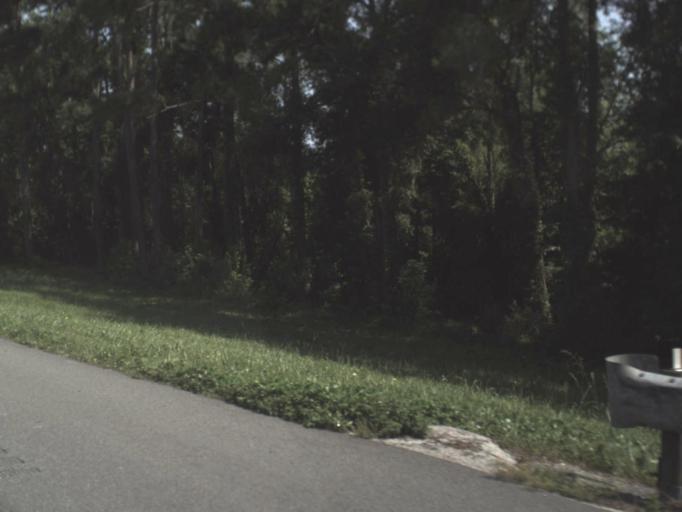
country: US
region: Florida
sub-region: Suwannee County
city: Wellborn
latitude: 30.3686
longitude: -82.8575
